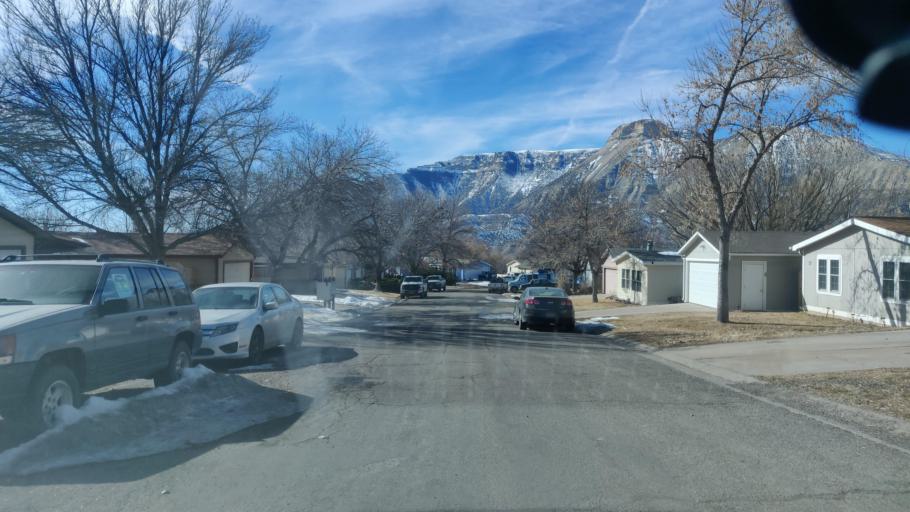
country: US
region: Colorado
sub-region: Garfield County
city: Parachute
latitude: 39.4268
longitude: -108.0469
